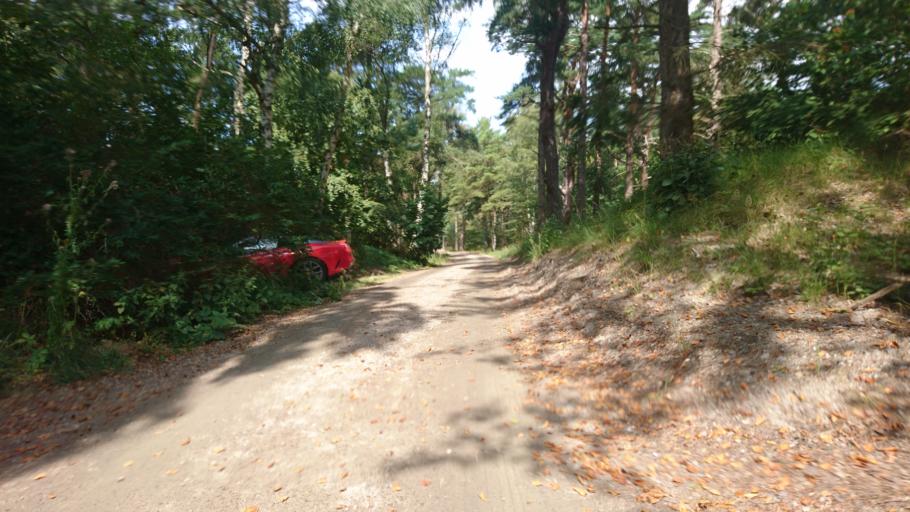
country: SE
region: Skane
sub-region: Vellinge Kommun
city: Ljunghusen
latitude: 55.3877
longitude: 12.9225
